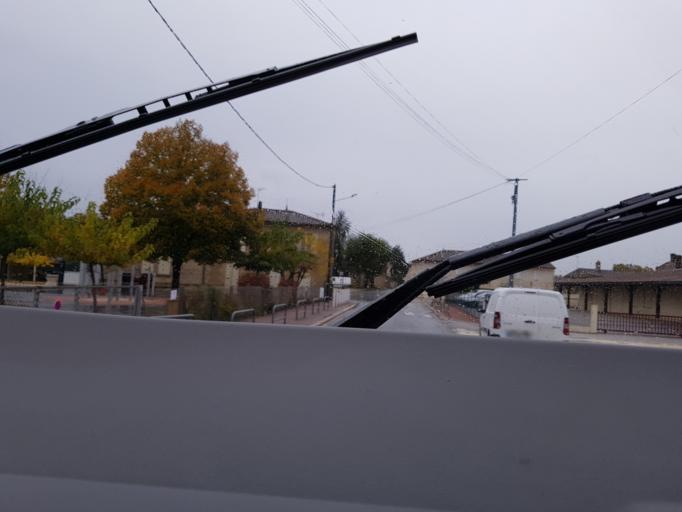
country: FR
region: Aquitaine
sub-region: Departement de la Gironde
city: Cezac
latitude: 45.1111
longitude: -0.4435
